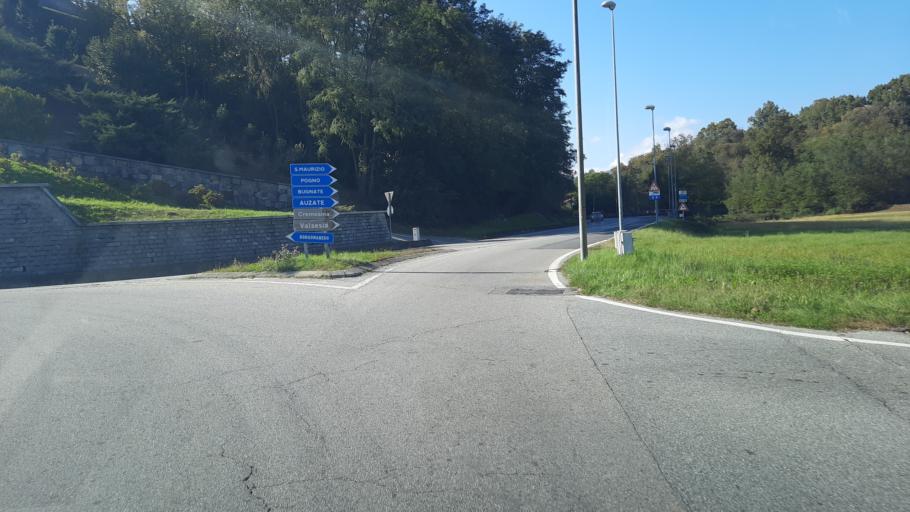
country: IT
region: Piedmont
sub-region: Provincia di Novara
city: Gozzano
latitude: 45.7383
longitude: 8.4318
